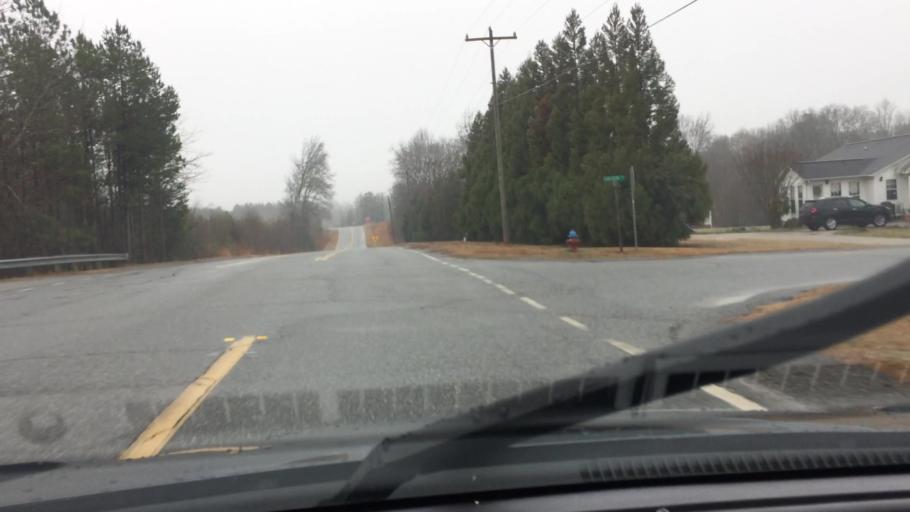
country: US
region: South Carolina
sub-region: Anderson County
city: Williamston
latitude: 34.6296
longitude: -82.4811
